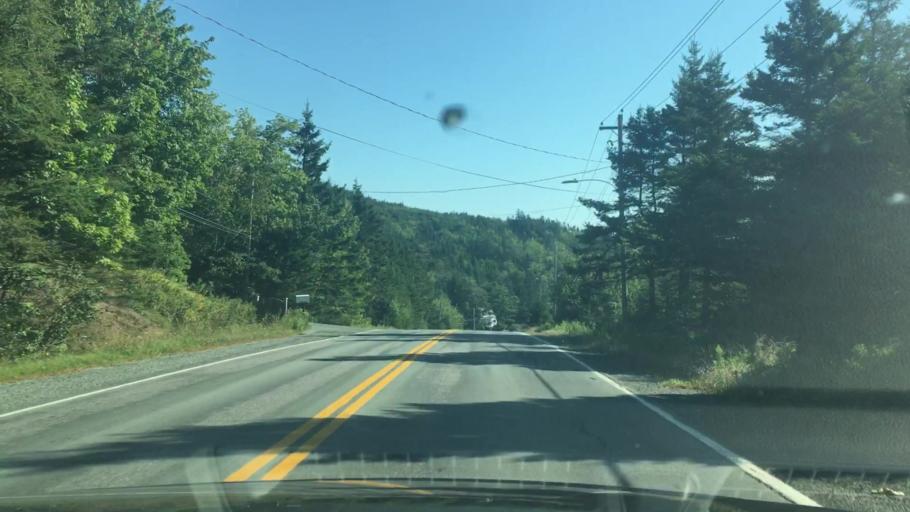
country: CA
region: Nova Scotia
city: Cole Harbour
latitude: 44.7775
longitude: -63.0650
